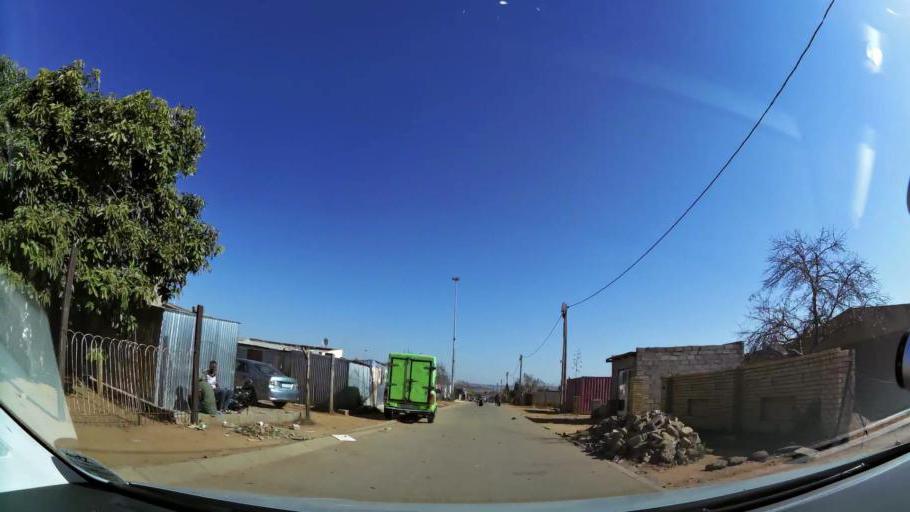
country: ZA
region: Gauteng
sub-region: Ekurhuleni Metropolitan Municipality
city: Tembisa
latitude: -26.0241
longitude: 28.2357
